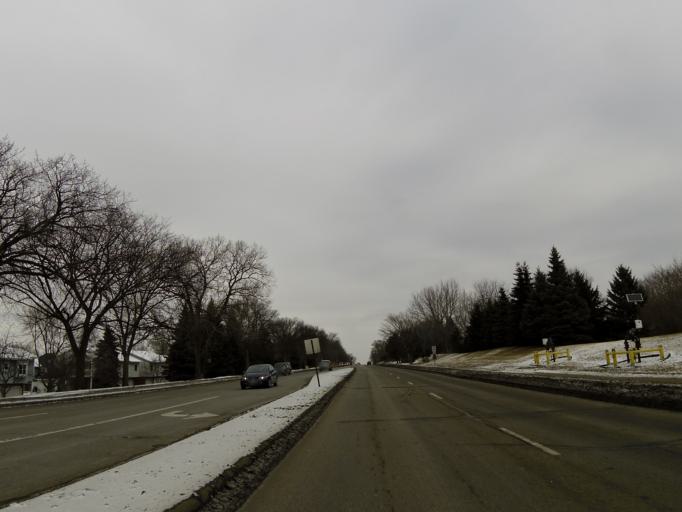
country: US
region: Minnesota
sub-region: Scott County
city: Savage
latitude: 44.8265
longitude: -93.3503
